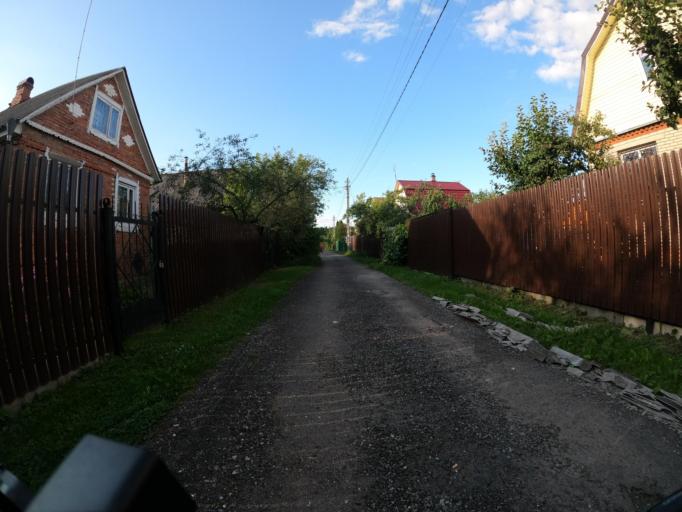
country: RU
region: Moskovskaya
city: Beloozerskiy
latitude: 55.4488
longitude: 38.5000
